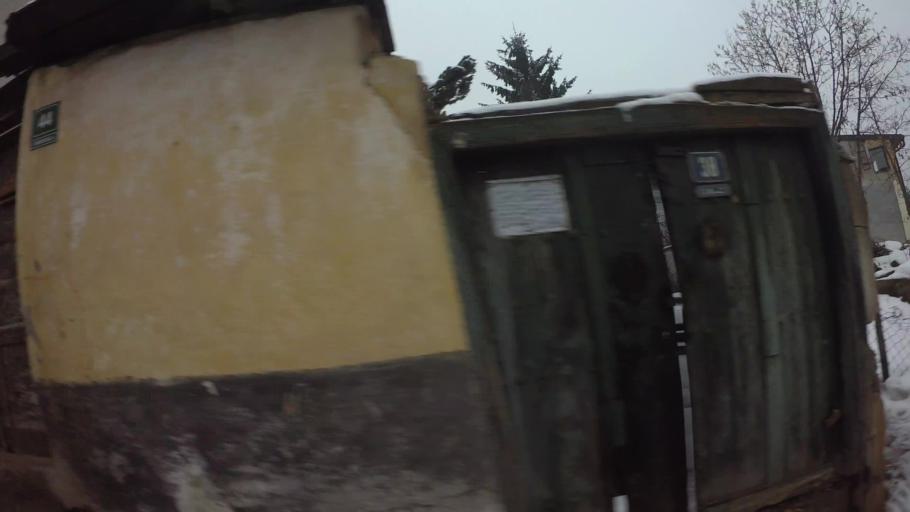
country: BA
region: Federation of Bosnia and Herzegovina
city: Kobilja Glava
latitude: 43.8518
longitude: 18.4334
